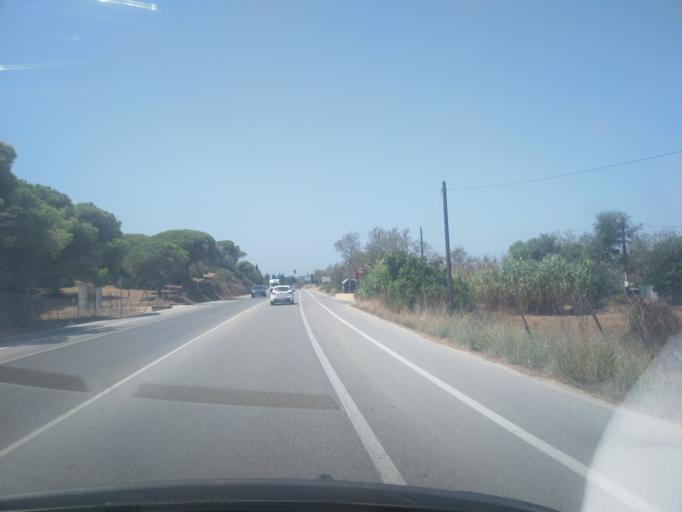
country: ES
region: Andalusia
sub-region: Provincia de Cadiz
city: Chiclana de la Frontera
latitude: 36.3891
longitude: -6.1395
